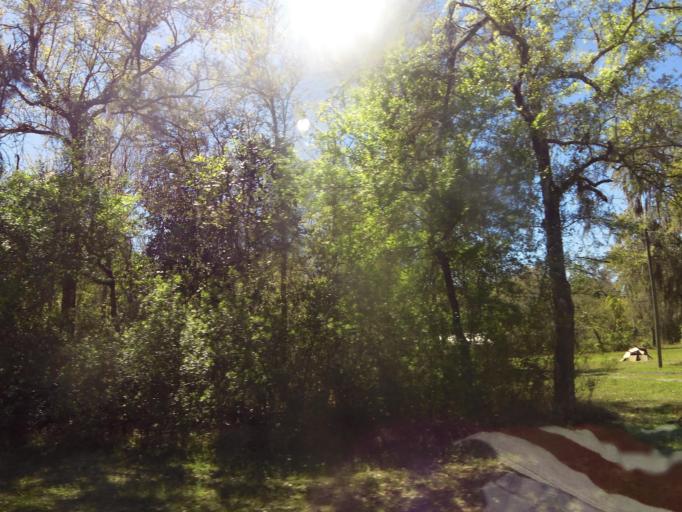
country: US
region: Florida
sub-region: Bradford County
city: Starke
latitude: 30.0480
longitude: -82.0656
